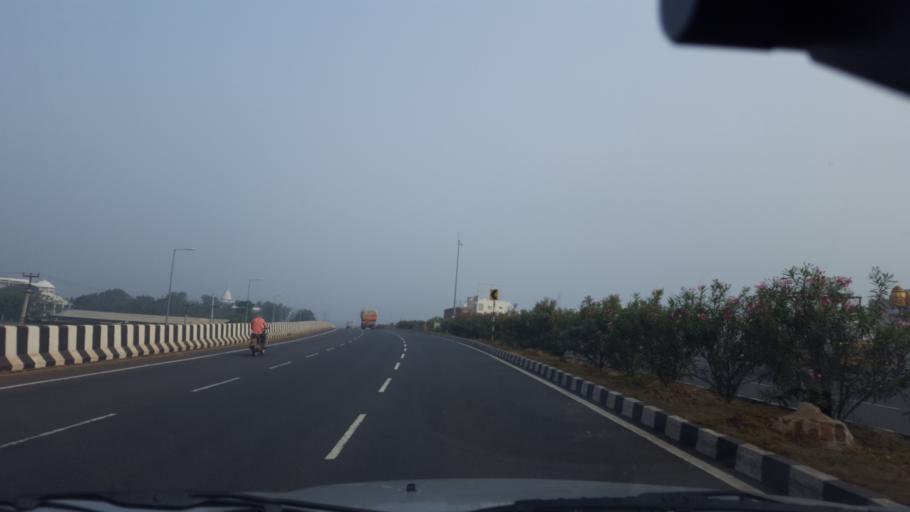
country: IN
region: Andhra Pradesh
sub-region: Prakasam
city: Ongole
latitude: 15.4565
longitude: 80.0479
